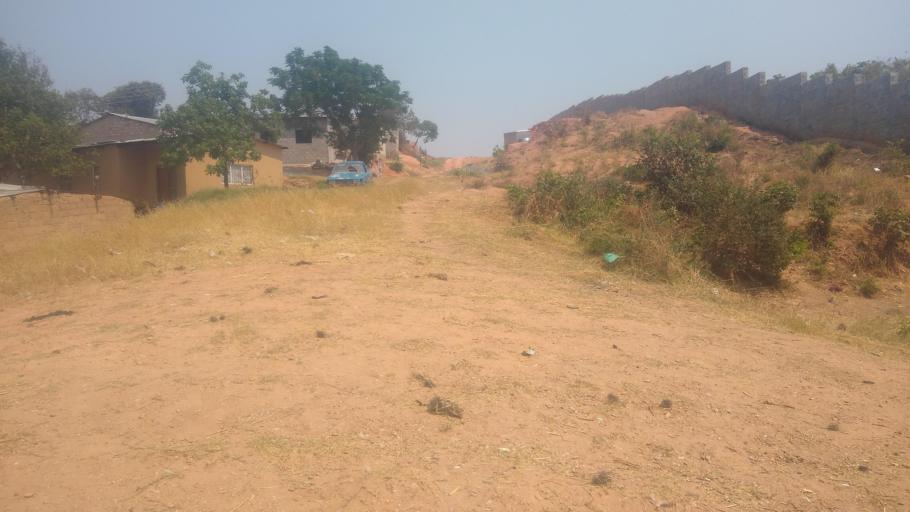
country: ZM
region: Lusaka
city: Lusaka
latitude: -15.4406
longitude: 28.3868
